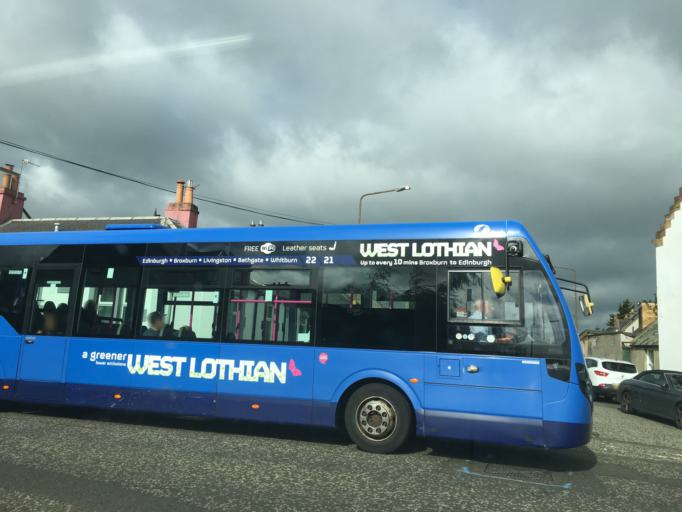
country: GB
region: Scotland
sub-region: Edinburgh
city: Newbridge
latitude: 55.9392
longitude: -3.4078
